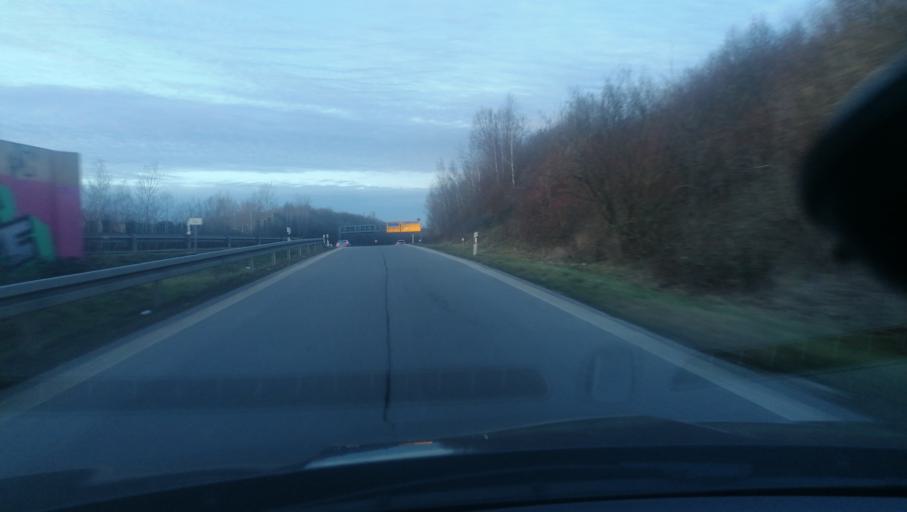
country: DE
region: North Rhine-Westphalia
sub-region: Regierungsbezirk Arnsberg
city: Dortmund
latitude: 51.4953
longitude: 7.5249
